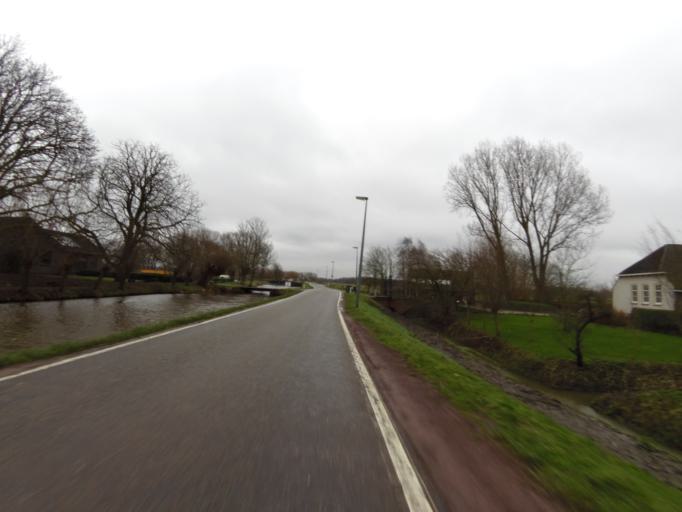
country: NL
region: South Holland
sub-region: Gemeente Maassluis
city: Maassluis
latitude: 51.9187
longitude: 4.2796
